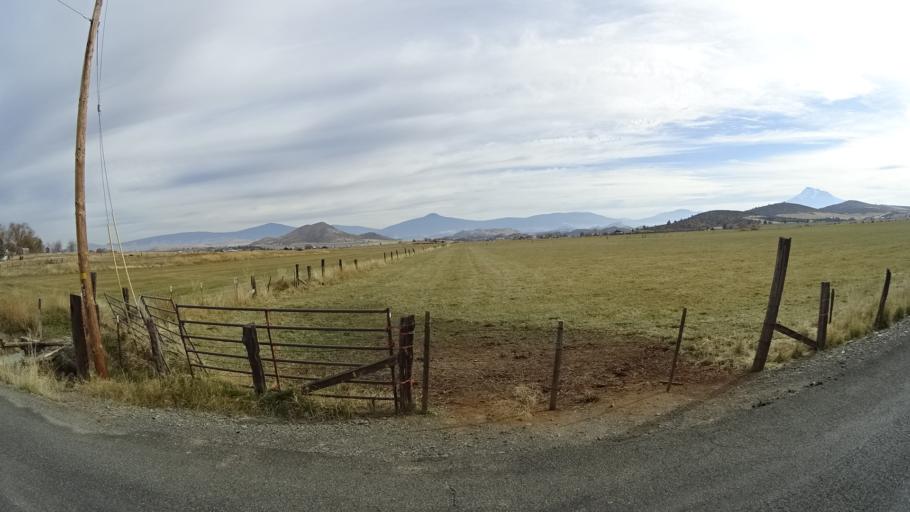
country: US
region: California
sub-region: Siskiyou County
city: Montague
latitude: 41.7017
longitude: -122.5640
